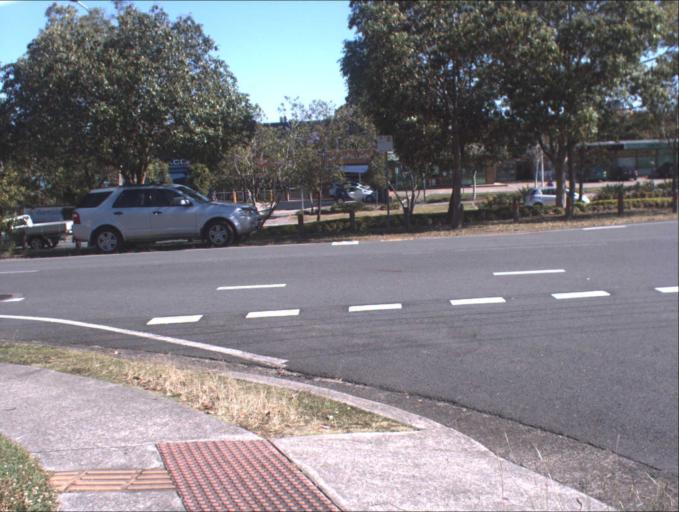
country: AU
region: Queensland
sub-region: Logan
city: Logan City
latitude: -27.6410
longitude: 153.1105
